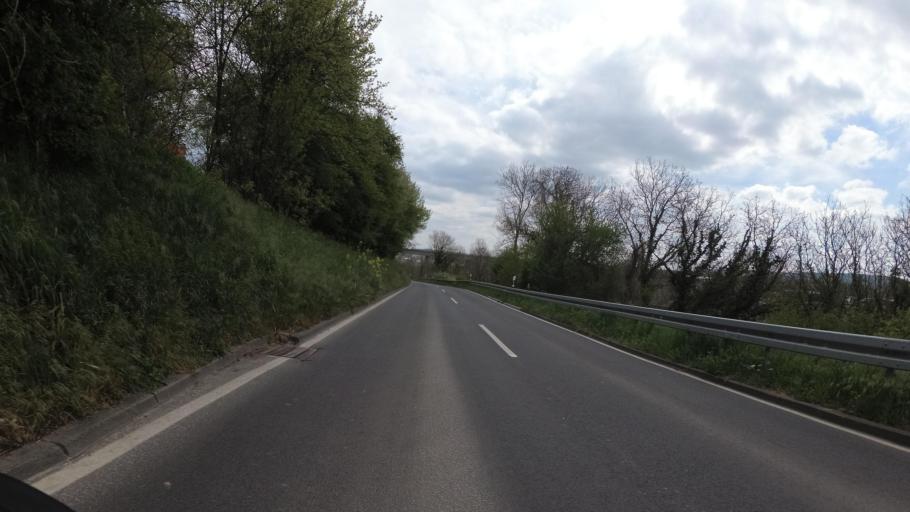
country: DE
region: Baden-Wuerttemberg
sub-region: Regierungsbezirk Stuttgart
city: Neuenstadt am Kocher
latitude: 49.2428
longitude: 9.3422
